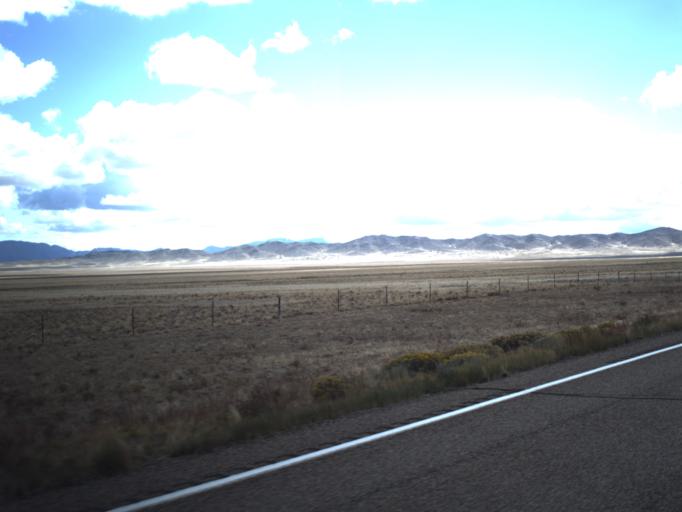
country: US
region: Utah
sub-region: Beaver County
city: Milford
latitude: 38.6911
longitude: -113.9005
